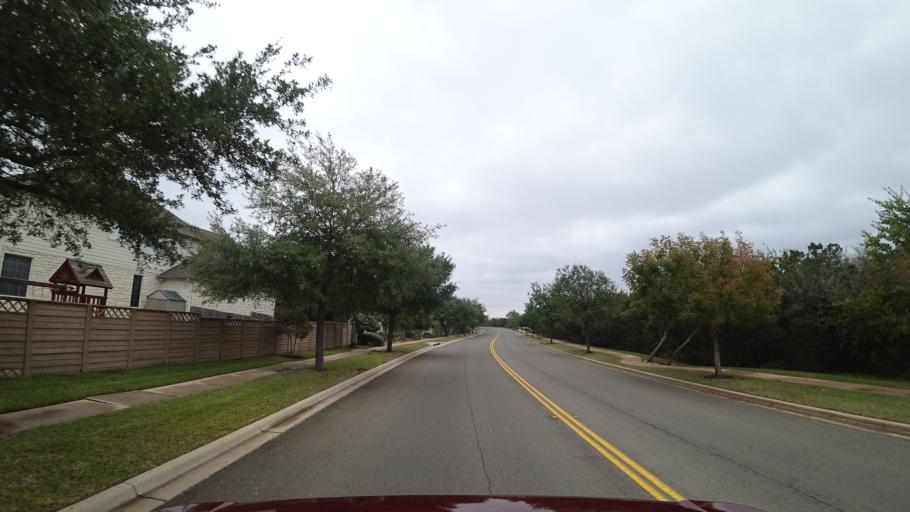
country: US
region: Texas
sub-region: Williamson County
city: Anderson Mill
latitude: 30.4308
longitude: -97.8350
